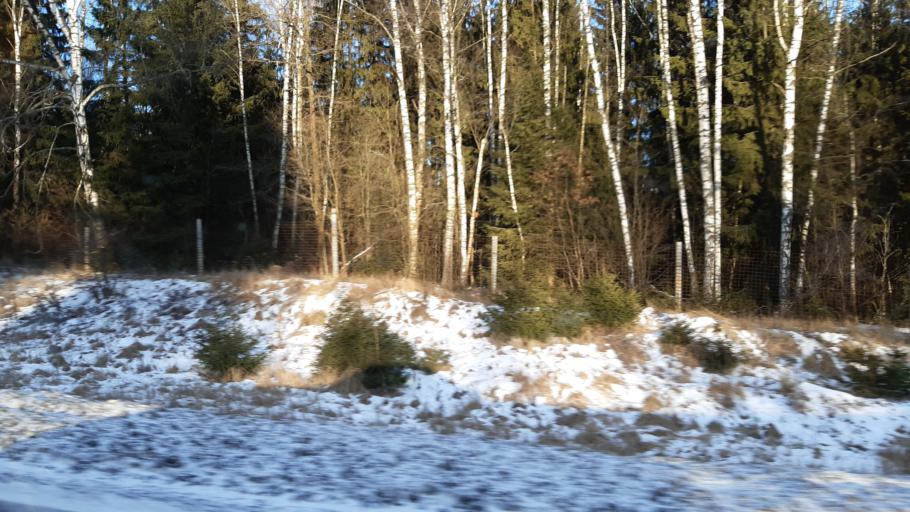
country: RU
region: Vladimir
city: Arsaki
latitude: 56.2790
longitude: 38.4045
